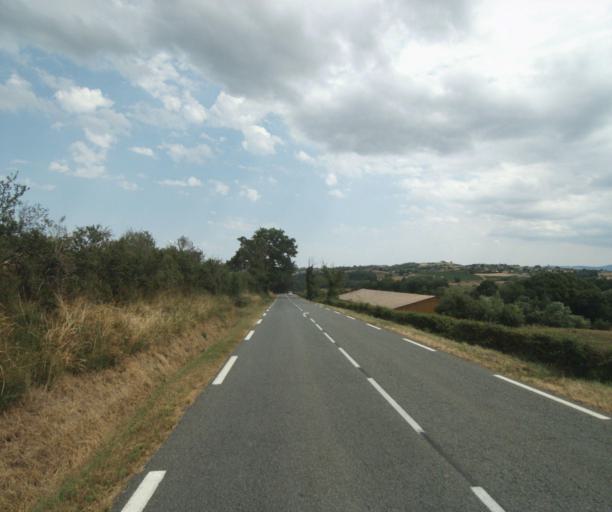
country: FR
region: Rhone-Alpes
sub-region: Departement du Rhone
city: Saint-Verand
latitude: 45.8959
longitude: 4.5509
